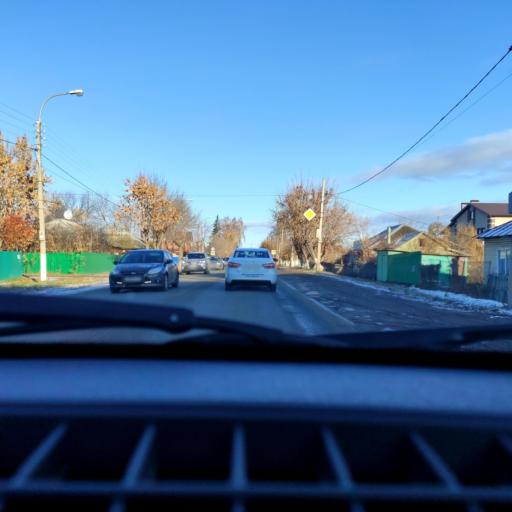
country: RU
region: Bashkortostan
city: Avdon
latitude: 54.7018
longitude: 55.8222
